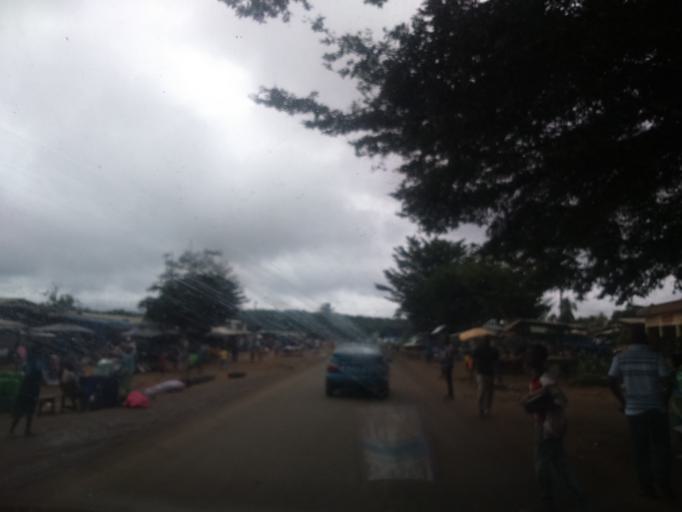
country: CI
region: Sud-Comoe
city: Bonoua
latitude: 5.2839
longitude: -3.5178
